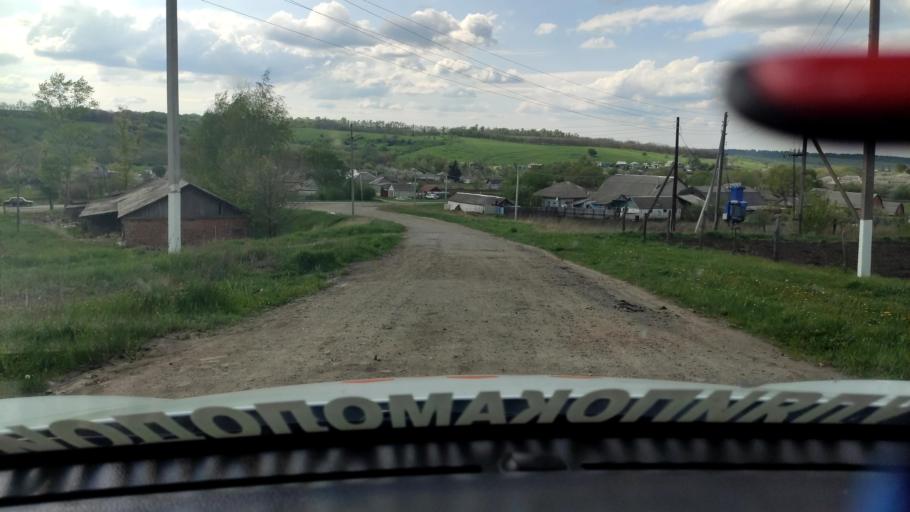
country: RU
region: Voronezj
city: Uryv-Pokrovka
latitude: 51.1218
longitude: 39.1647
